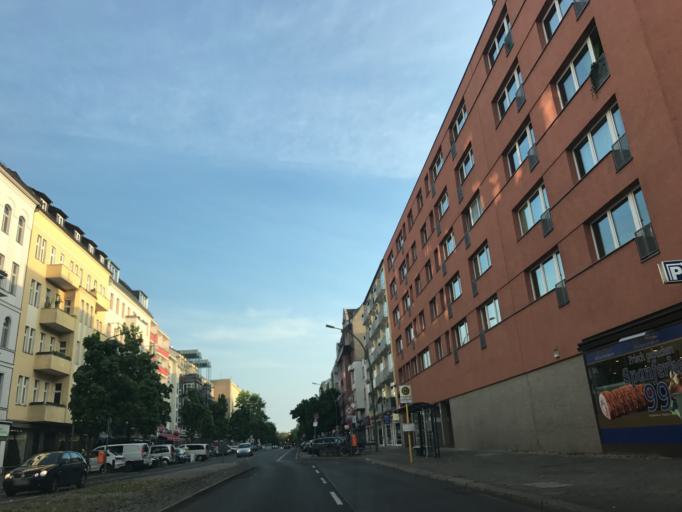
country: DE
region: Berlin
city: Wilmersdorf Bezirk
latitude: 52.4915
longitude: 13.3232
